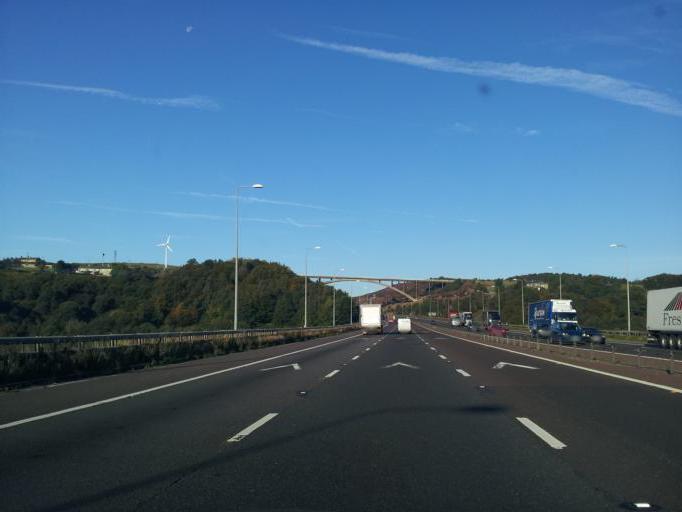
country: GB
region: England
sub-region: Calderdale
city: Ripponden
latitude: 53.6468
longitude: -1.9219
